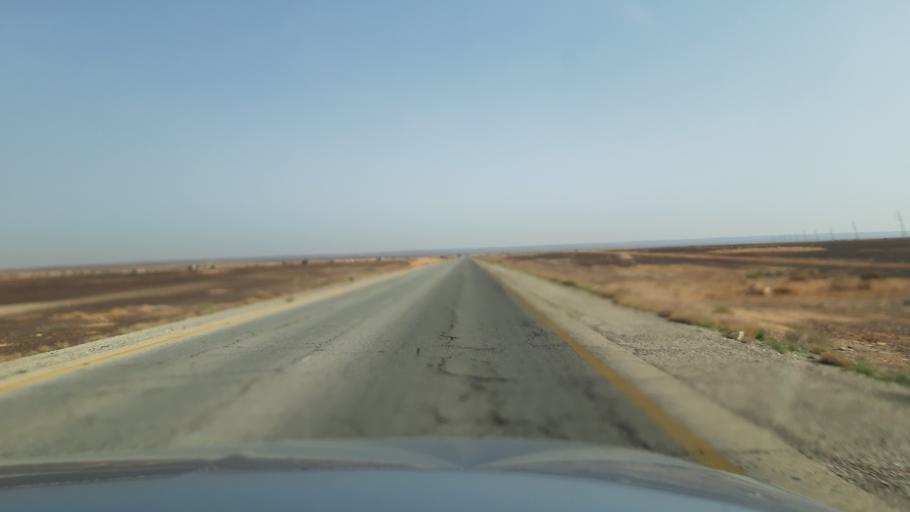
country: JO
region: Amman
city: Al Azraq ash Shamali
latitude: 31.7888
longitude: 36.5813
